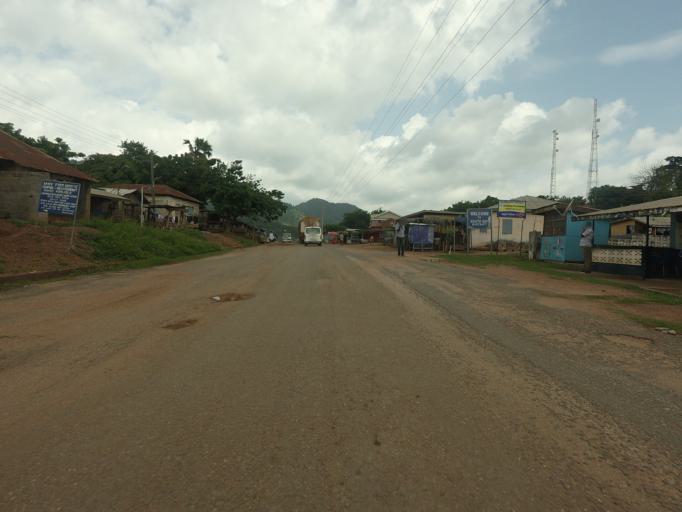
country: GH
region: Volta
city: Ho
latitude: 6.6884
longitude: 0.3333
